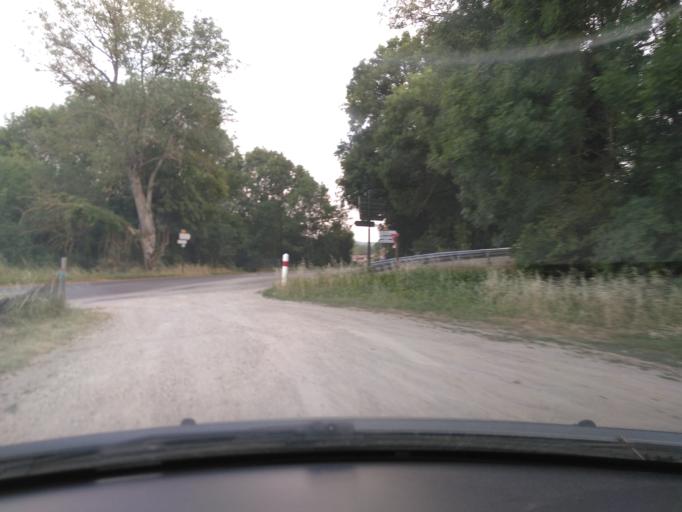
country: FR
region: Rhone-Alpes
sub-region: Departement de l'Isere
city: Beaurepaire
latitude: 45.4021
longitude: 5.1290
